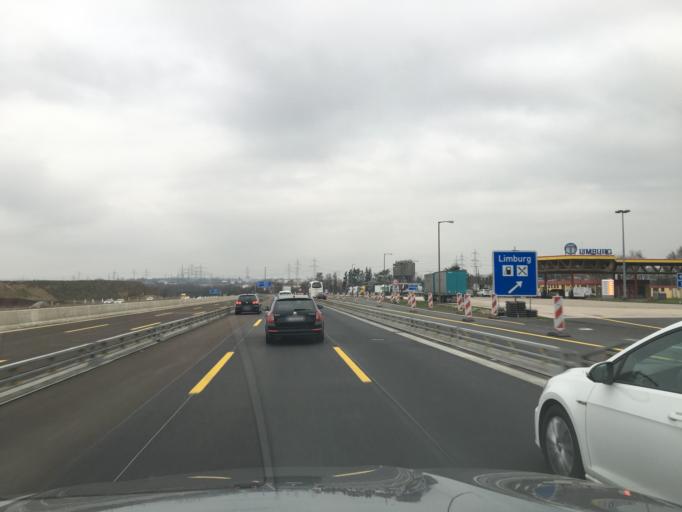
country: DE
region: Hesse
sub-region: Regierungsbezirk Giessen
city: Limburg an der Lahn
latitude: 50.3936
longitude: 8.0777
